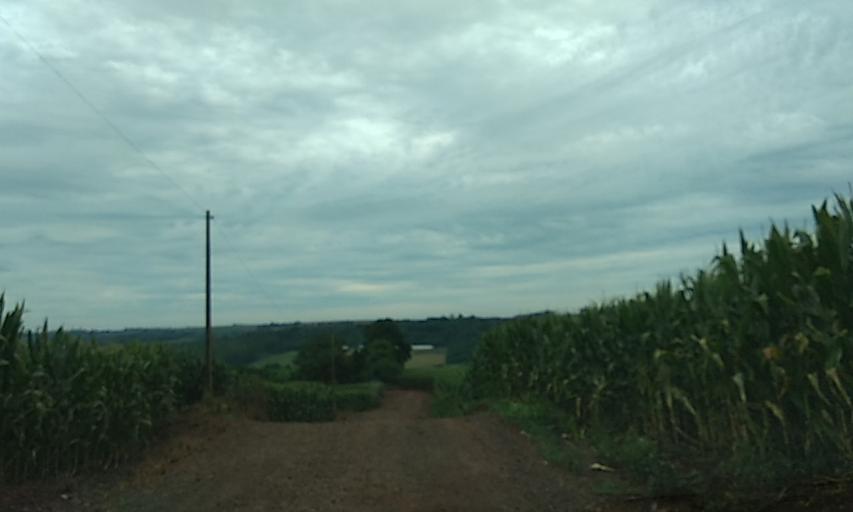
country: BR
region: Parana
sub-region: Marechal Candido Rondon
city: Marechal Candido Rondon
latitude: -24.5249
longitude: -54.0828
